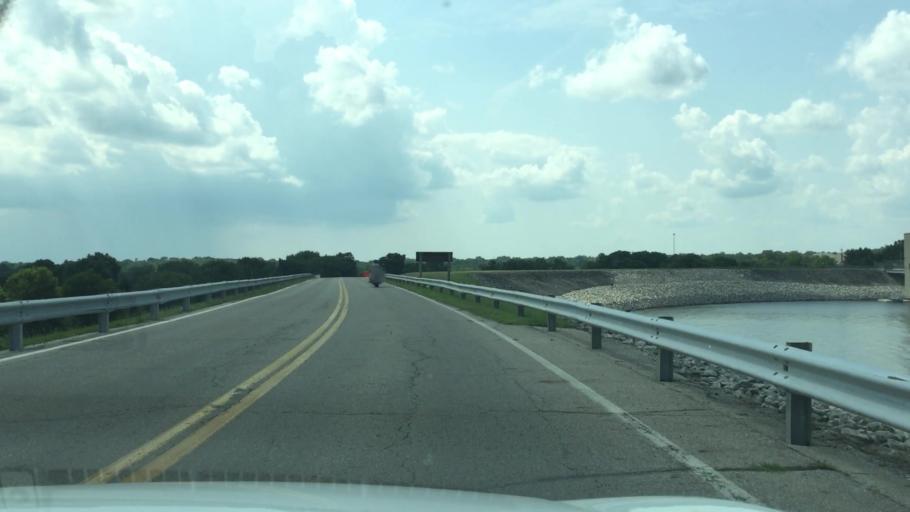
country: US
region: Ohio
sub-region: Clark County
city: Northridge
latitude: 39.9472
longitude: -83.7440
